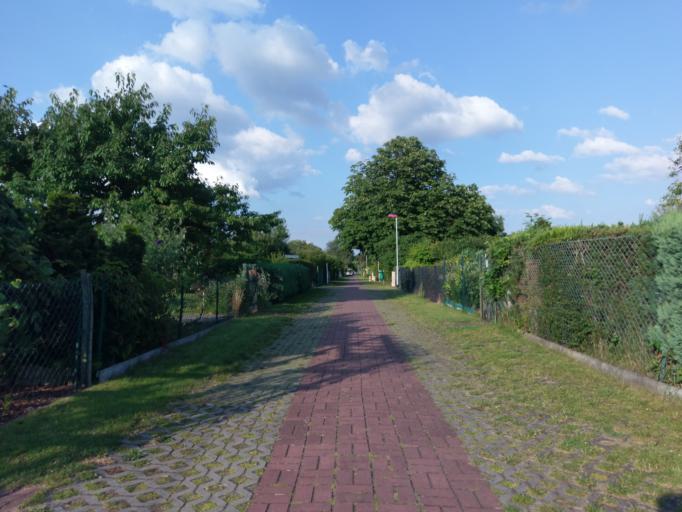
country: DE
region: Berlin
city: Lichterfelde
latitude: 52.4246
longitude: 13.2865
